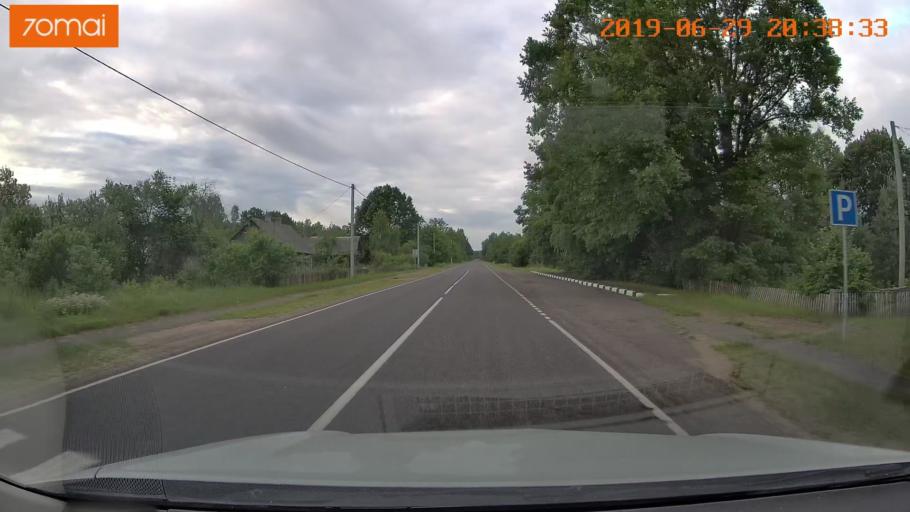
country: BY
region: Brest
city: Hantsavichy
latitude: 52.5513
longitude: 26.3644
